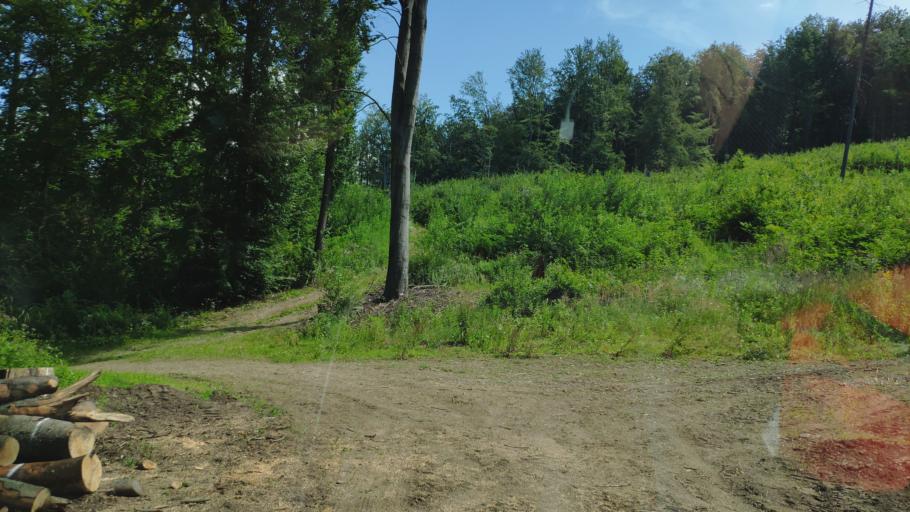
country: SK
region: Kosicky
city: Dobsina
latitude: 48.7148
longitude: 20.3859
